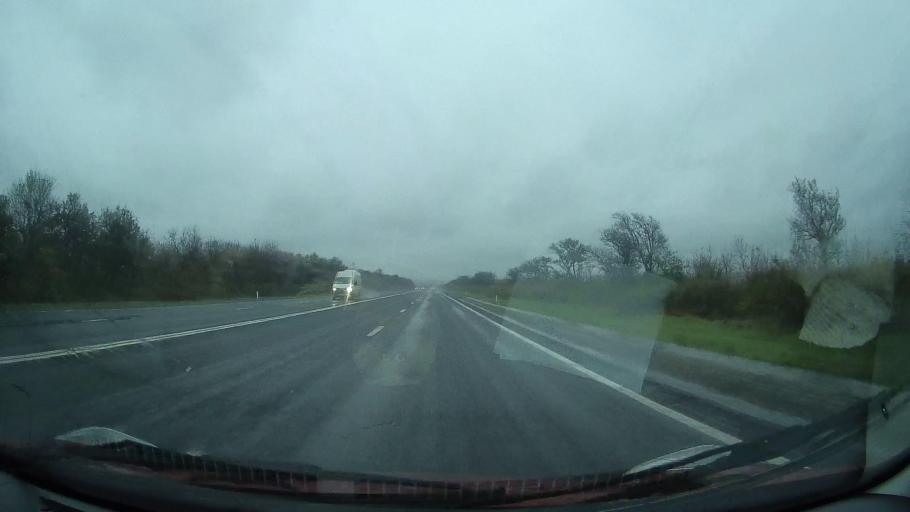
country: RU
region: Stavropol'skiy
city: Nevinnomyssk
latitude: 44.6170
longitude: 42.1022
